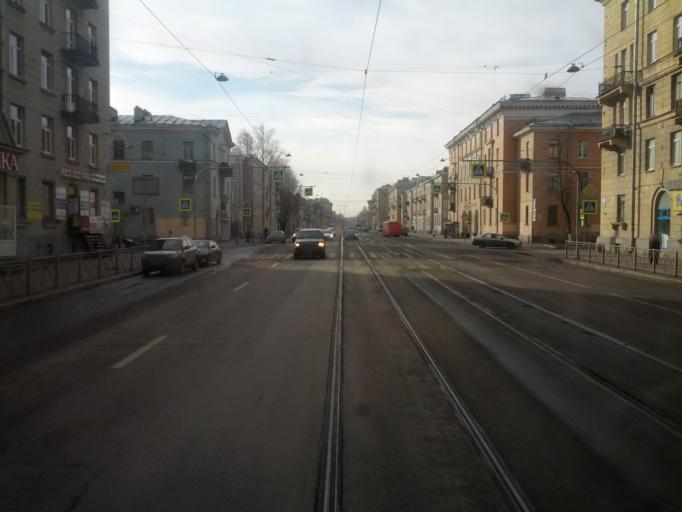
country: RU
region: Leningrad
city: Kalininskiy
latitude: 59.9581
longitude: 30.4156
